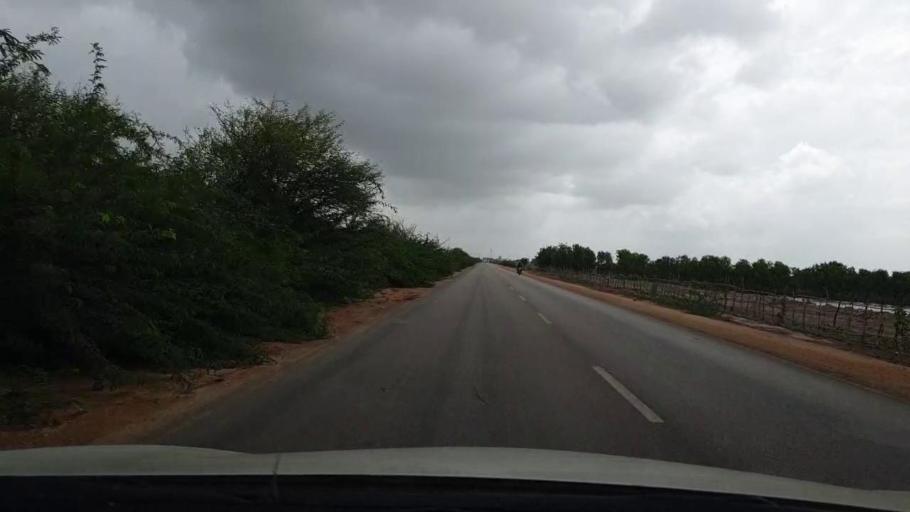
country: PK
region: Sindh
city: Mirpur Batoro
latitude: 24.6040
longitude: 68.2395
